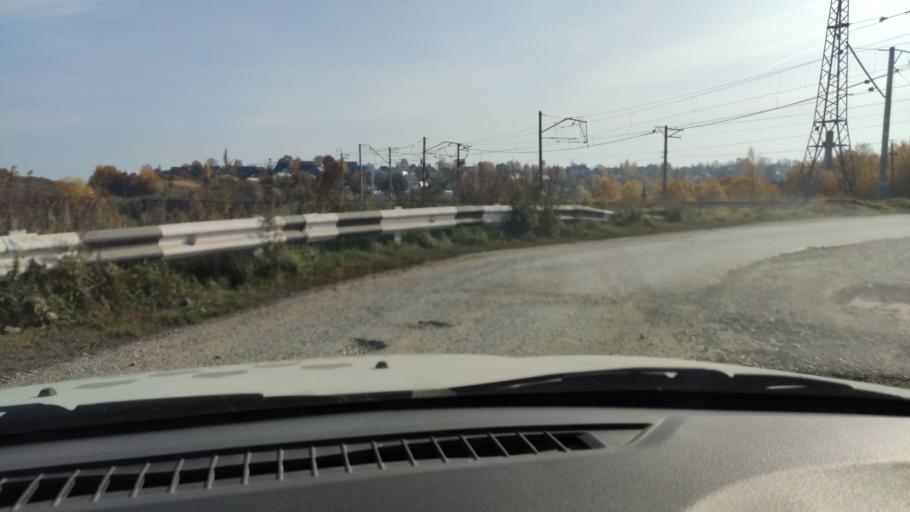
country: RU
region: Perm
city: Sylva
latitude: 58.0423
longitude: 56.7499
